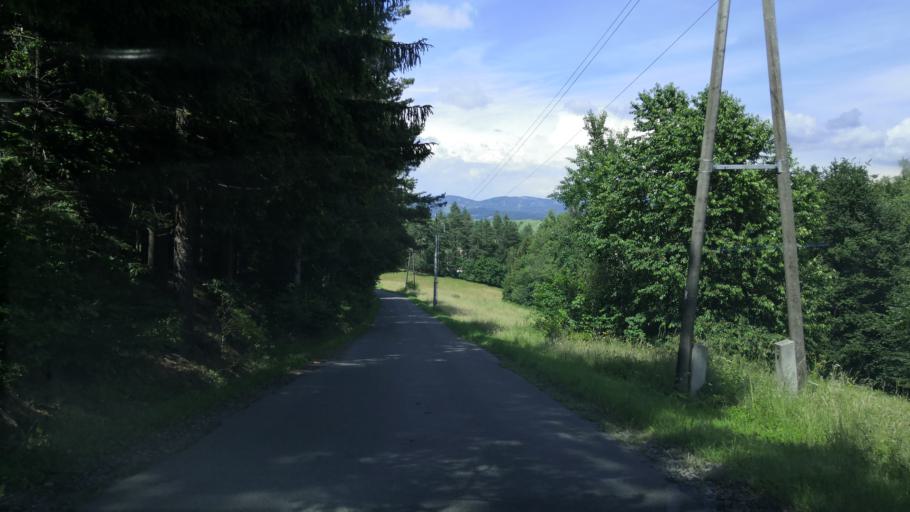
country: CZ
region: Zlin
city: Vidce
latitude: 49.4337
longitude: 18.0944
